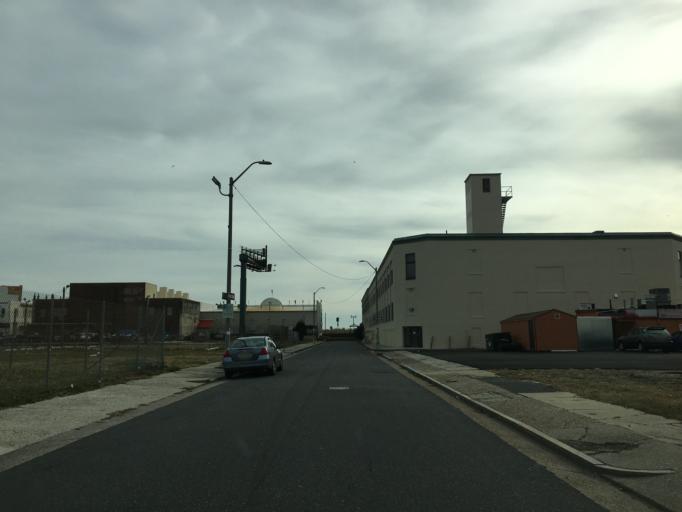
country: US
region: New Jersey
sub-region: Atlantic County
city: Atlantic City
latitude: 39.3587
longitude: -74.4252
